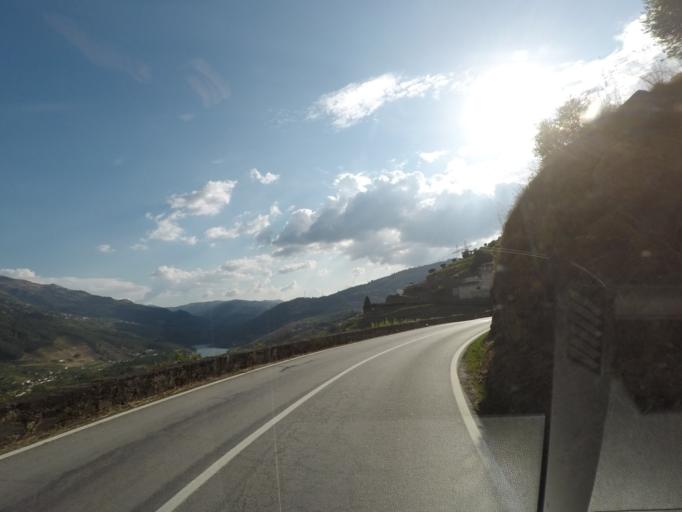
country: PT
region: Vila Real
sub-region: Mesao Frio
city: Mesao Frio
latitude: 41.1609
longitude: -7.8765
